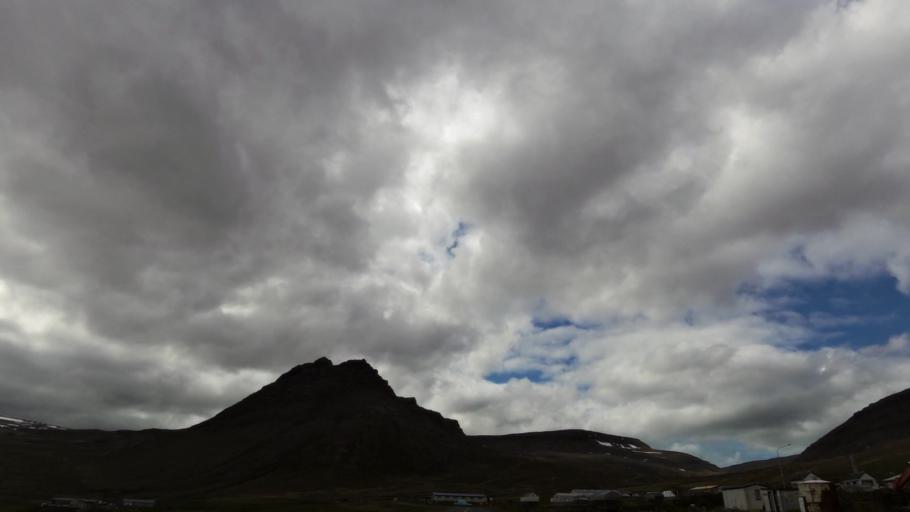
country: IS
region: Westfjords
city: Isafjoerdur
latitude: 66.1587
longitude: -23.2780
